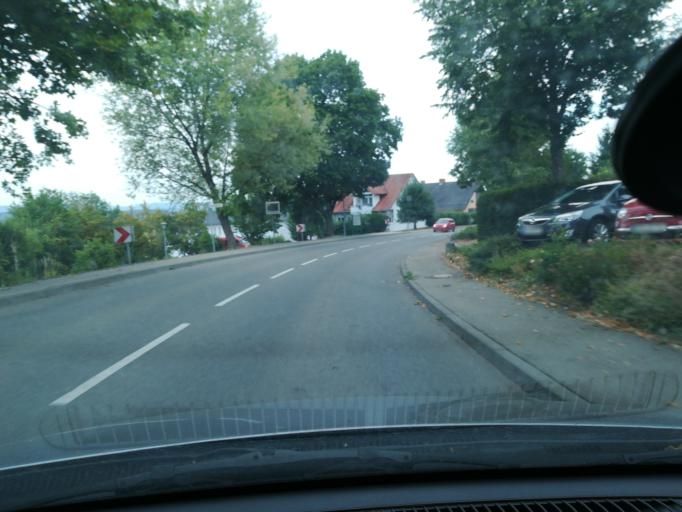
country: DE
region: Baden-Wuerttemberg
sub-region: Freiburg Region
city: Muhlhausen-Ehingen
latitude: 47.8093
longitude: 8.8172
